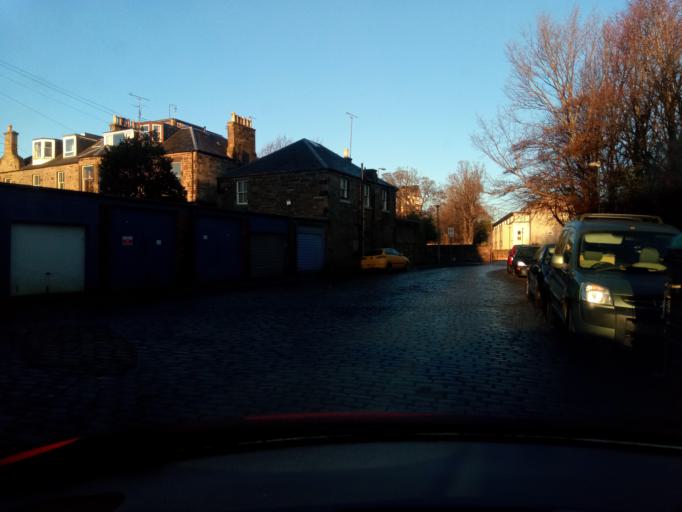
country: GB
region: Scotland
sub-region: Edinburgh
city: Edinburgh
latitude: 55.9727
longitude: -3.1919
